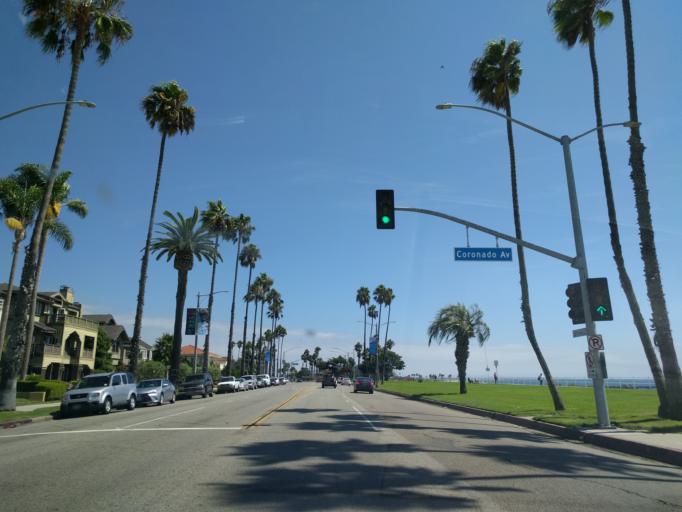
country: US
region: California
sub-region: Los Angeles County
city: Long Beach
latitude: 33.7614
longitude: -118.1545
